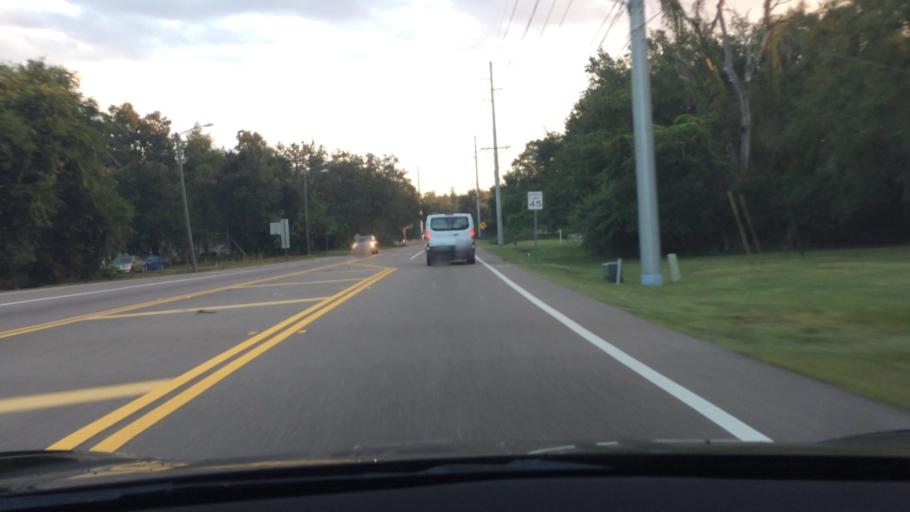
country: US
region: Florida
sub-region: Hillsborough County
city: Citrus Park
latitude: 28.1033
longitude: -82.5804
